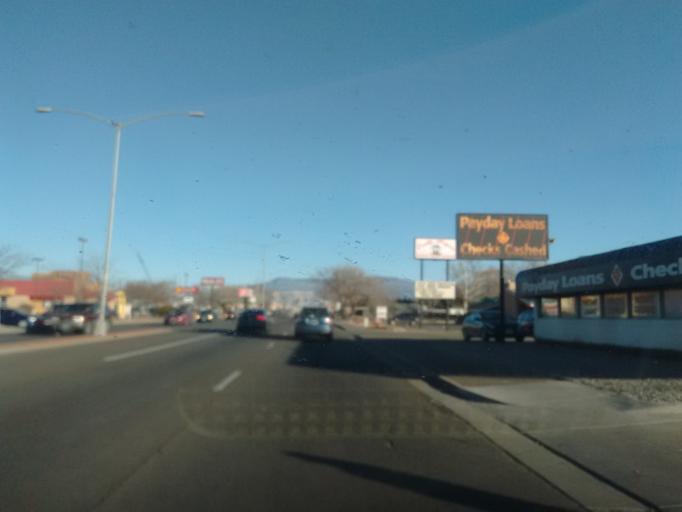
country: US
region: Colorado
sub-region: Mesa County
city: Grand Junction
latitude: 39.0773
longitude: -108.5272
